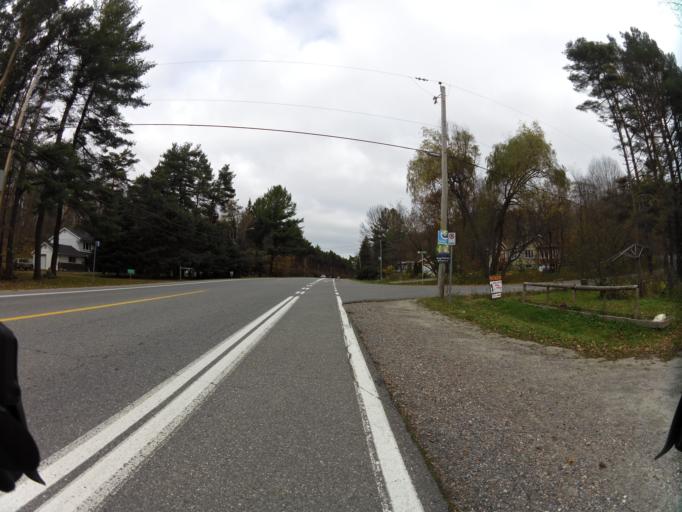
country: CA
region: Quebec
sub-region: Outaouais
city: Gatineau
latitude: 45.5185
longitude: -75.8085
